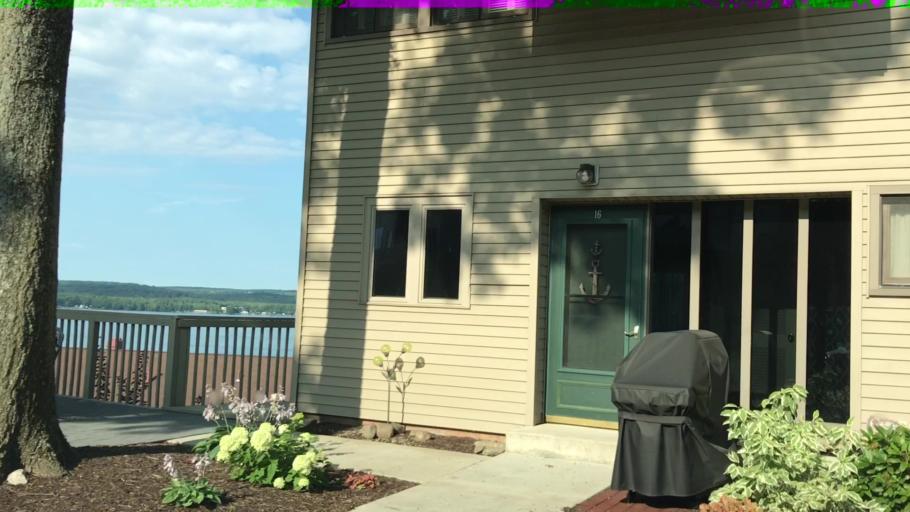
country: US
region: New York
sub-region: Chautauqua County
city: Mayville
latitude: 42.2476
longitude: -79.4639
